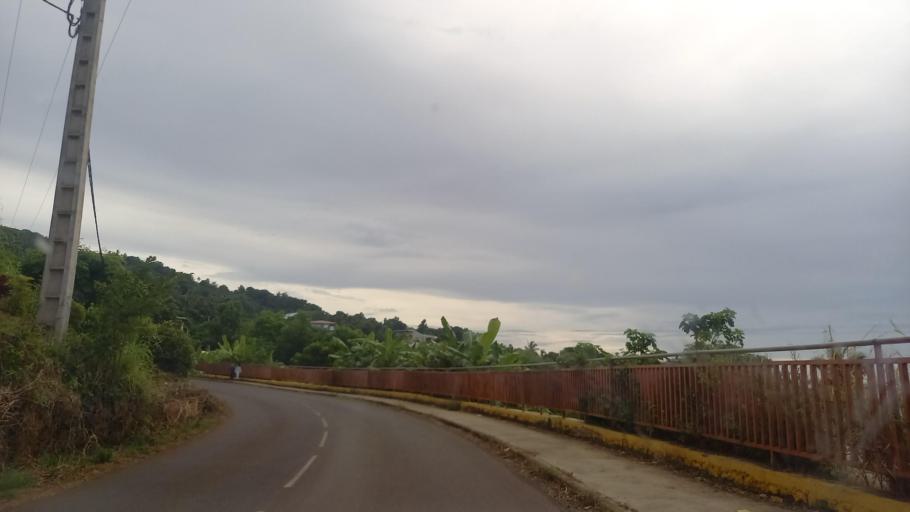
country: YT
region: Boueni
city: Boueni
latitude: -12.9006
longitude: 45.0972
